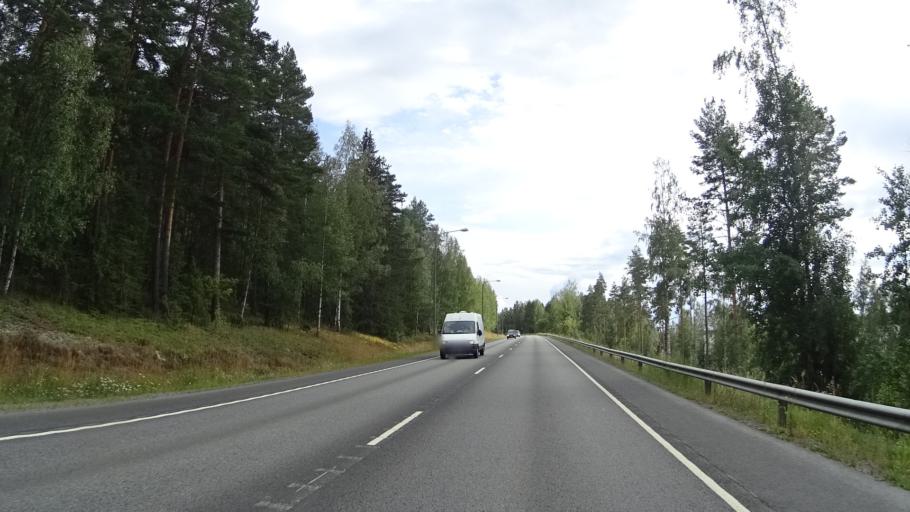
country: FI
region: Pirkanmaa
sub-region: Tampere
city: Kangasala
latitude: 61.4350
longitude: 24.1261
